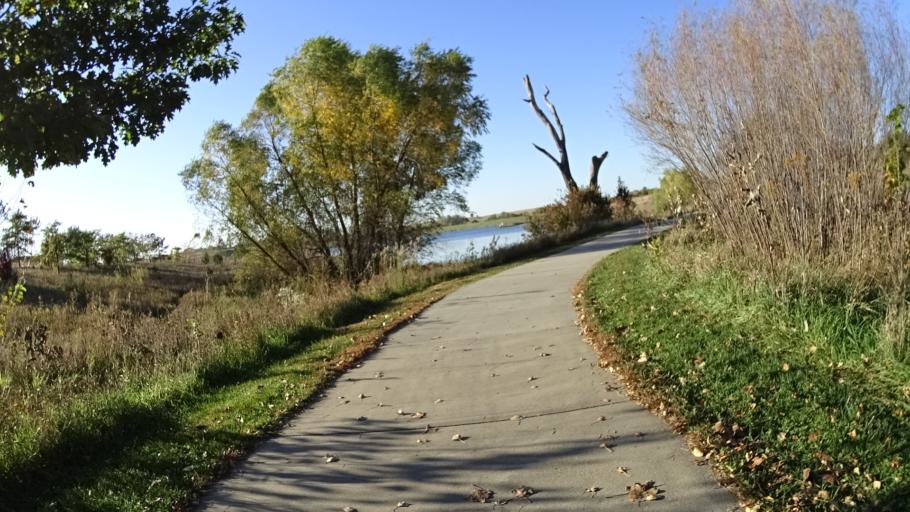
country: US
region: Nebraska
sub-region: Sarpy County
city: Papillion
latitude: 41.1406
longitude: -96.0645
